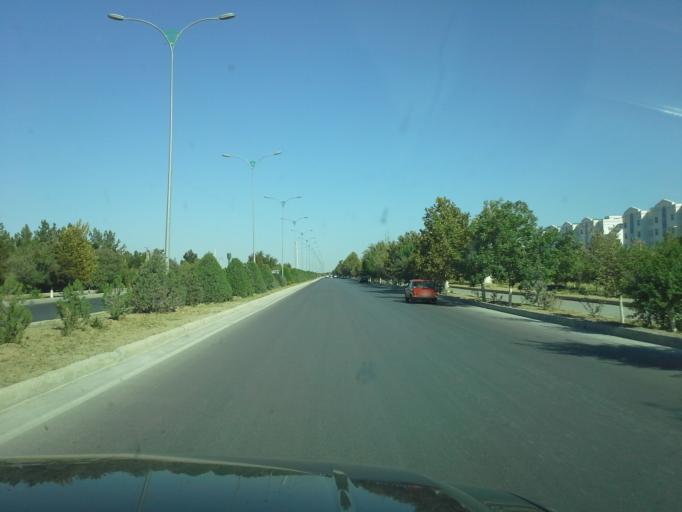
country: TM
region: Ahal
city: Abadan
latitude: 38.1650
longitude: 57.9372
